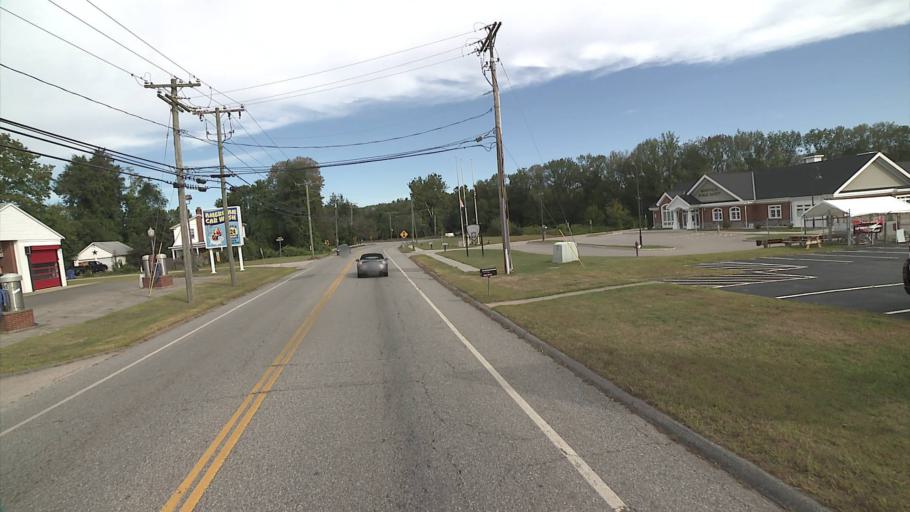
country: US
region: Connecticut
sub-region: New London County
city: Uncasville
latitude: 41.4505
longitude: -72.1068
